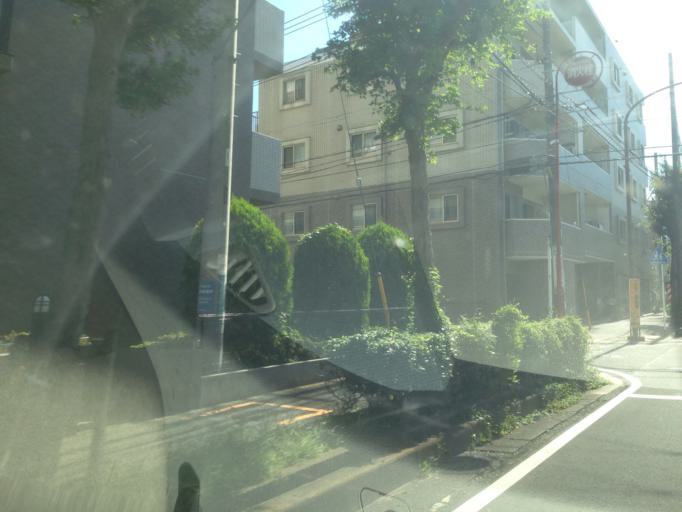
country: JP
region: Tokyo
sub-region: Machida-shi
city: Machida
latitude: 35.5700
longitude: 139.4024
